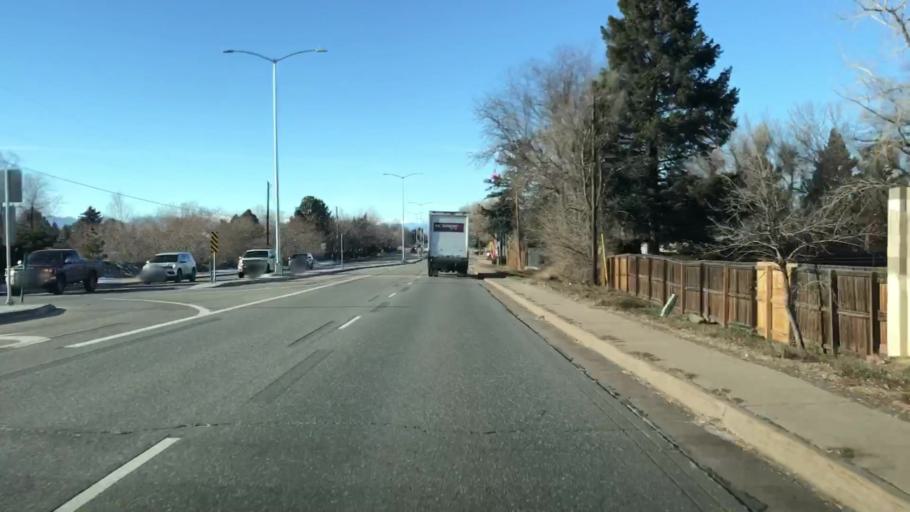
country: US
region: Colorado
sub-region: Arapahoe County
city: Glendale
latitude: 39.6820
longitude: -104.8797
